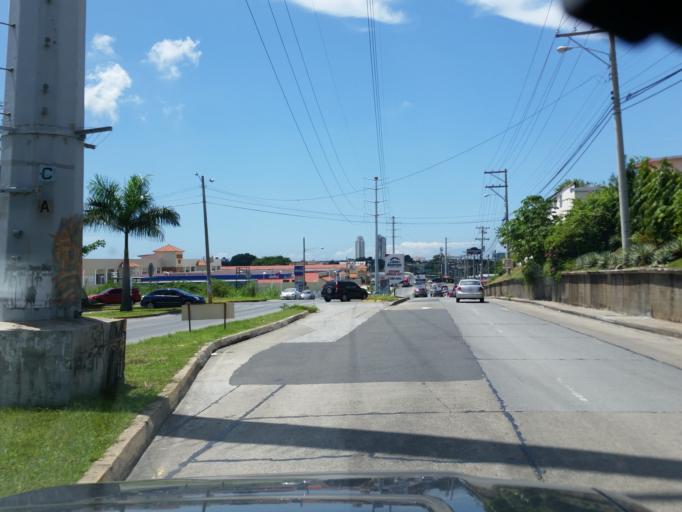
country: PA
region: Panama
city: San Miguelito
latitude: 9.0530
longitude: -79.4610
